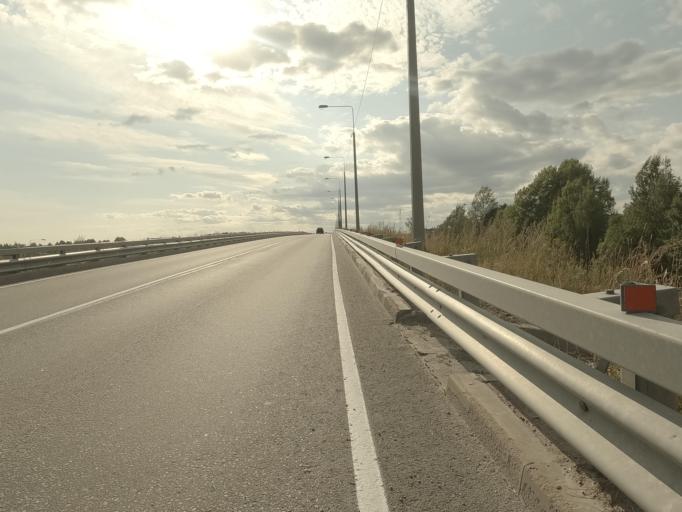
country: RU
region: Leningrad
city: Lesogorskiy
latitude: 60.8567
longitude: 28.9517
